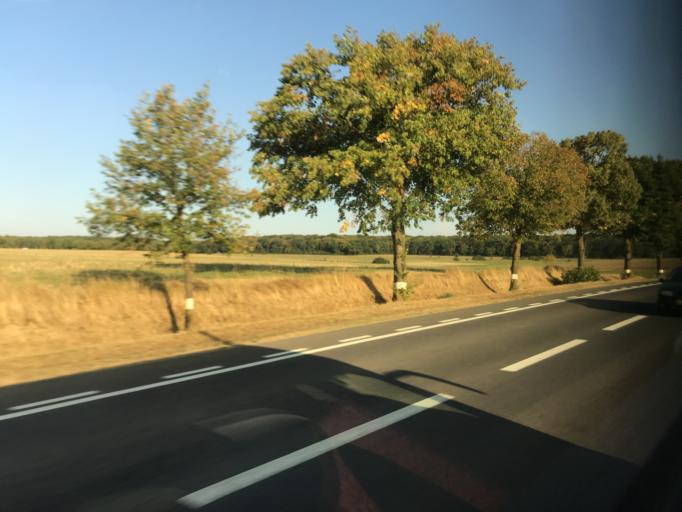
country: LU
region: Luxembourg
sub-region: Canton de Luxembourg
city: Alzingen
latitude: 49.5558
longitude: 6.1694
